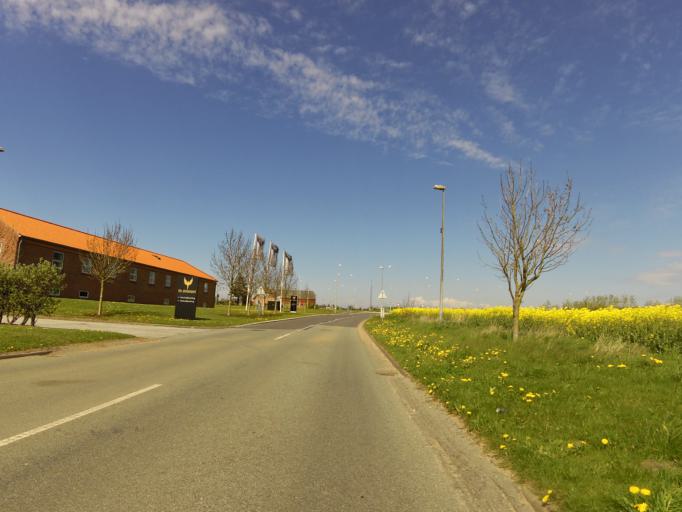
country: DK
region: South Denmark
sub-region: Tonder Kommune
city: Sherrebek
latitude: 55.1533
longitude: 8.7828
